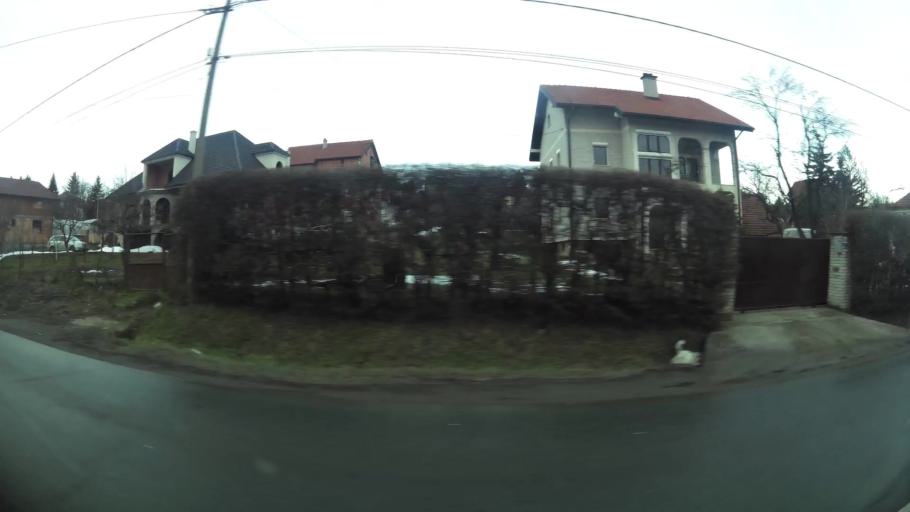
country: RS
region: Central Serbia
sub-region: Belgrade
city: Vozdovac
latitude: 44.7431
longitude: 20.4818
